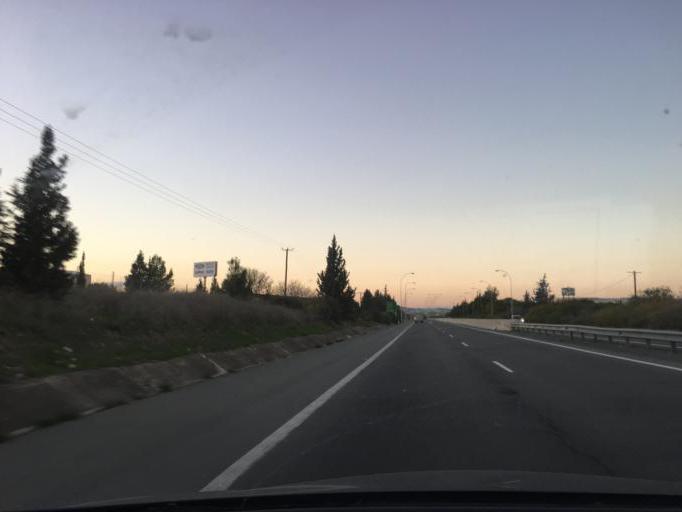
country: CY
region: Larnaka
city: Dhromolaxia
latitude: 34.9004
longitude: 33.5730
